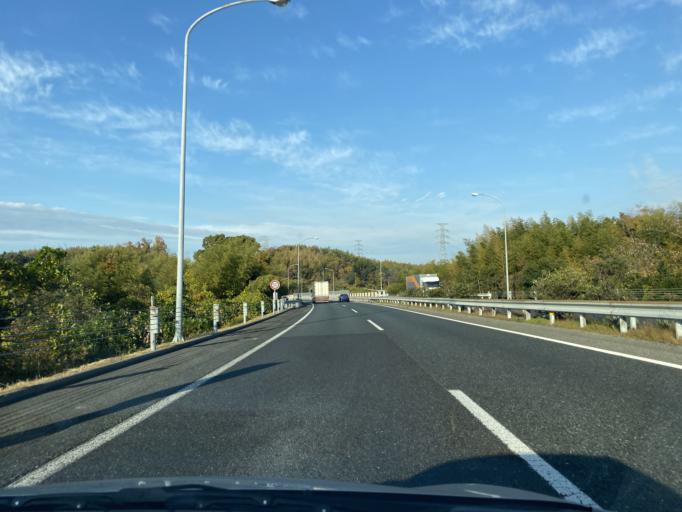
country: JP
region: Osaka
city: Izumi
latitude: 34.4102
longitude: 135.4482
